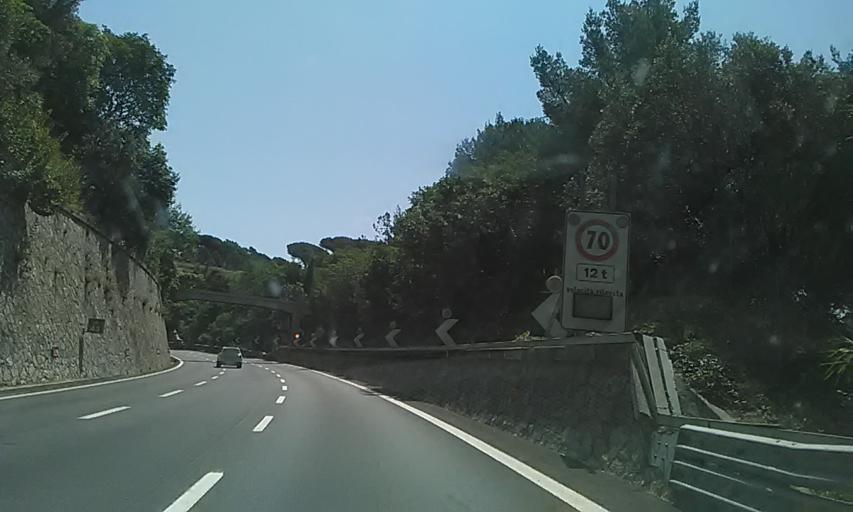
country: IT
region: Liguria
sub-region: Provincia di Savona
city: Albisola Superiore
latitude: 44.3350
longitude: 8.5270
